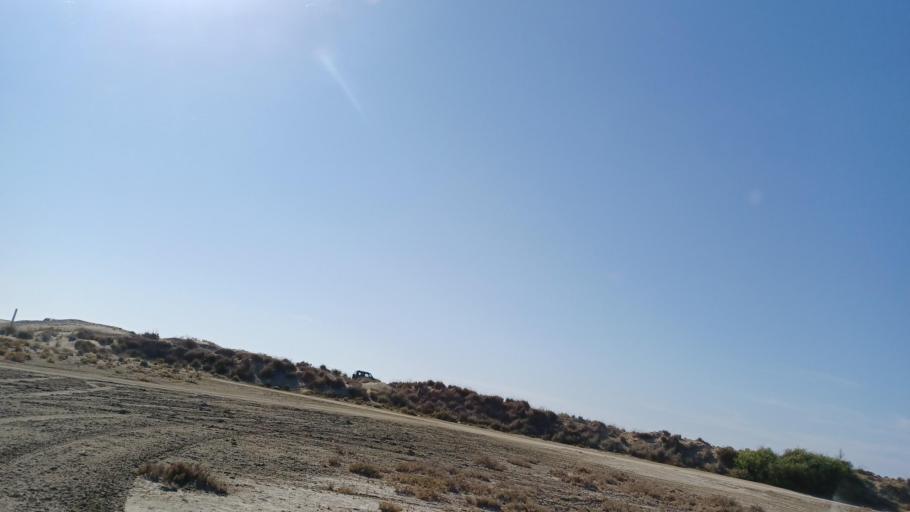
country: CY
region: Larnaka
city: Kolossi
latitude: 34.6026
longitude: 32.9329
